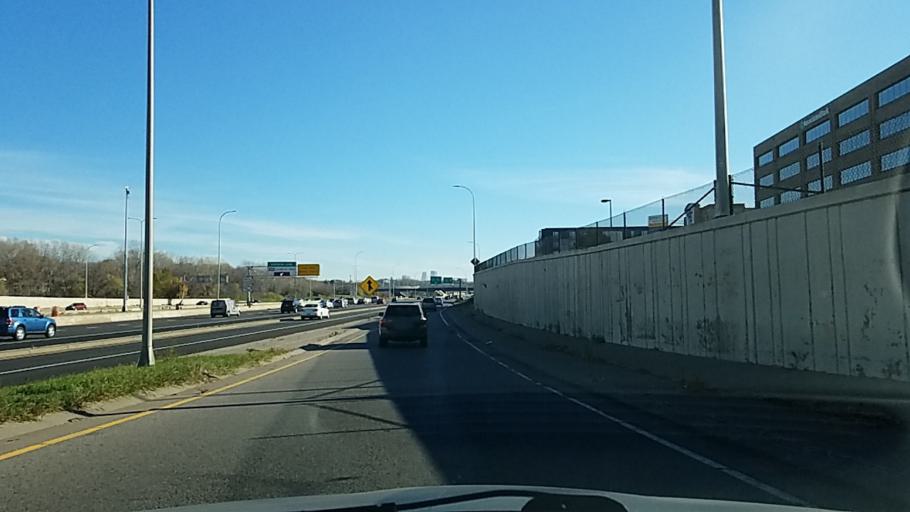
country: US
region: Minnesota
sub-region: Hennepin County
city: Saint Louis Park
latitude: 44.9701
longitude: -93.3497
